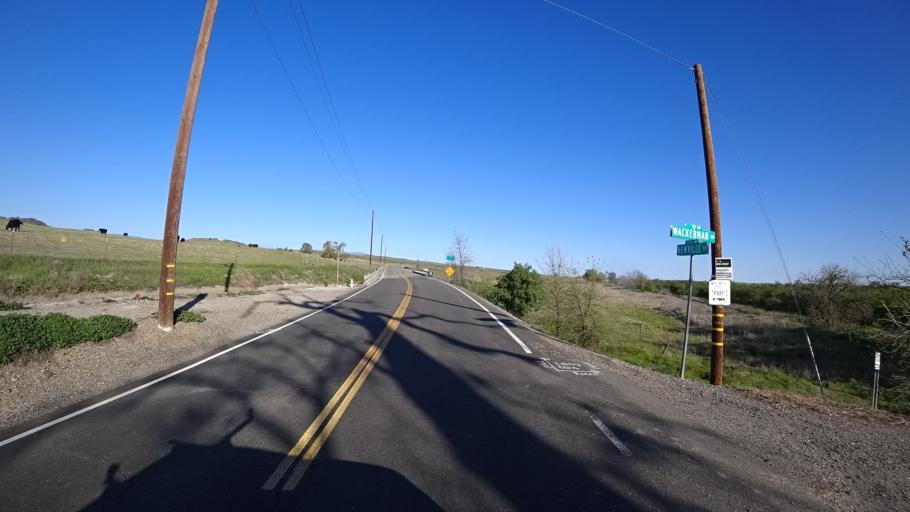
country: US
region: California
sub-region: Glenn County
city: Orland
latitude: 39.7990
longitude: -122.3199
